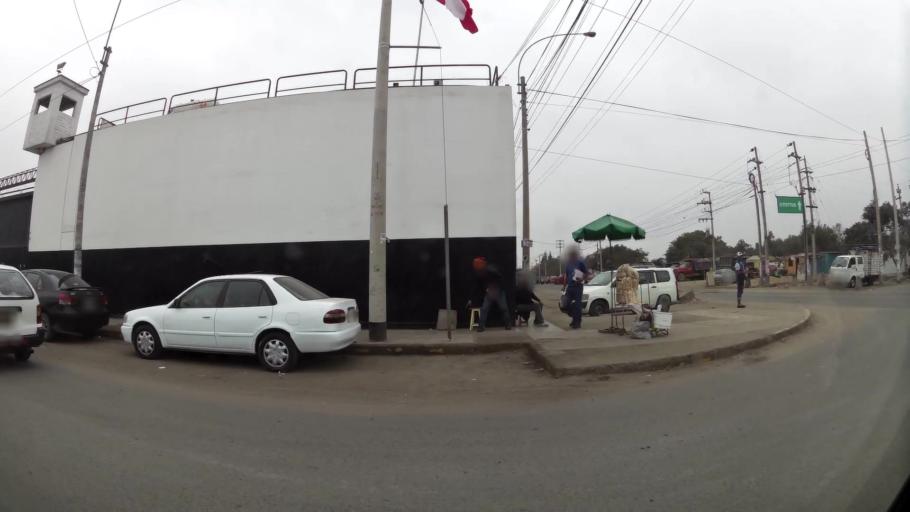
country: PE
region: Lima
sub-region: Lima
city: Surco
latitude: -12.1764
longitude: -76.9759
